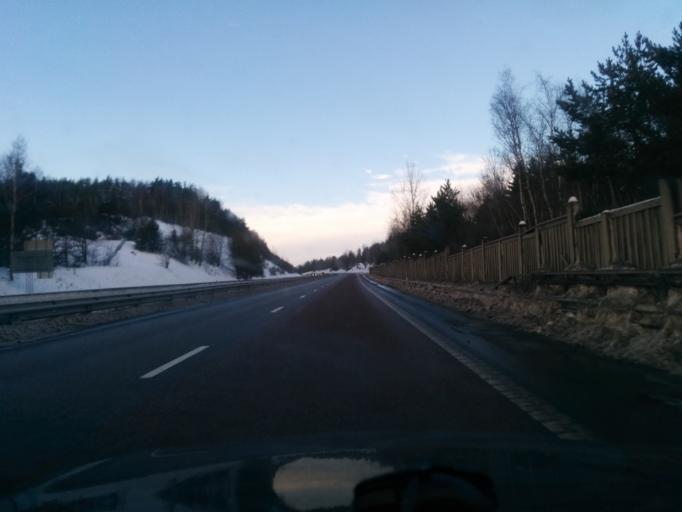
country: SE
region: Uppsala
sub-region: Habo Kommun
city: Balsta
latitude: 59.5733
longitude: 17.5461
